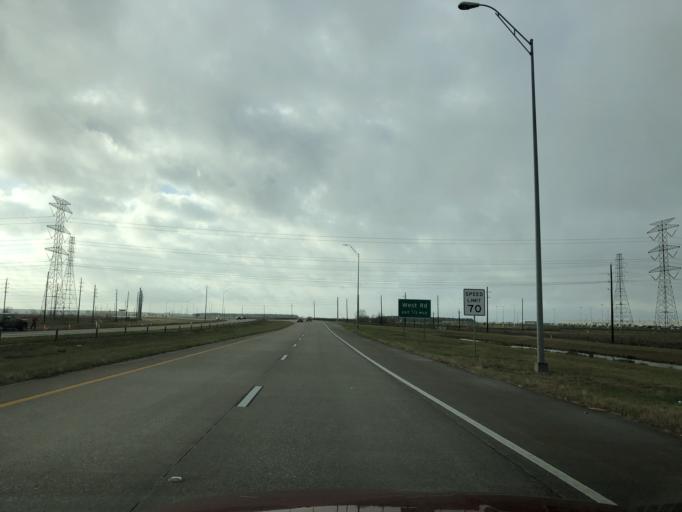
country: US
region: Texas
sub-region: Harris County
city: Cypress
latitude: 29.9149
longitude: -95.7619
